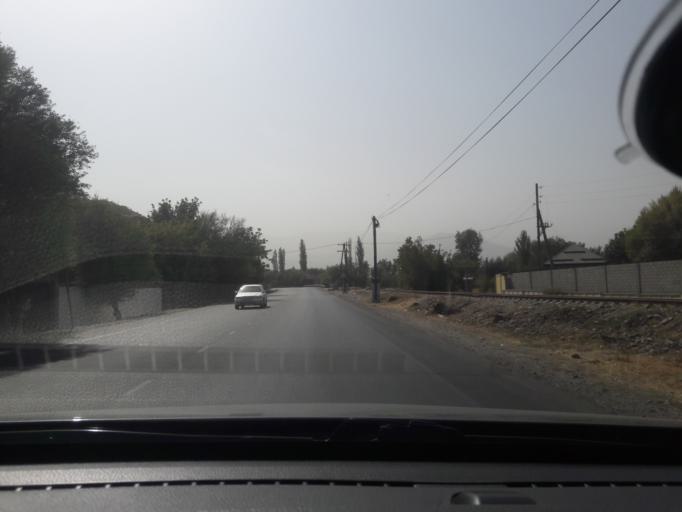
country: TJ
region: Republican Subordination
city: Vahdat
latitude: 38.5218
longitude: 69.0284
